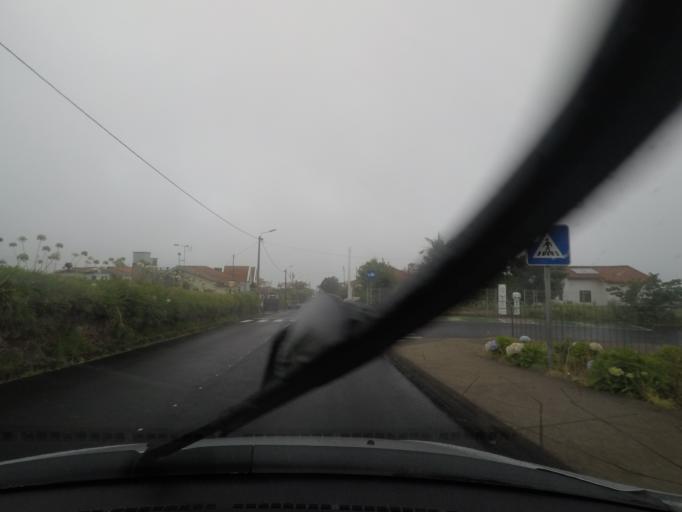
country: PT
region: Madeira
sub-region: Santana
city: Santana
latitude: 32.8030
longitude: -16.8811
